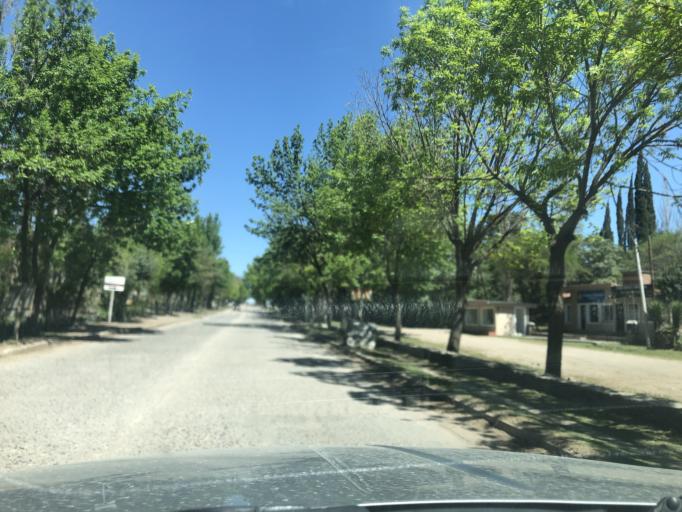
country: AR
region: Cordoba
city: La Granja
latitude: -31.0209
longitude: -64.2743
